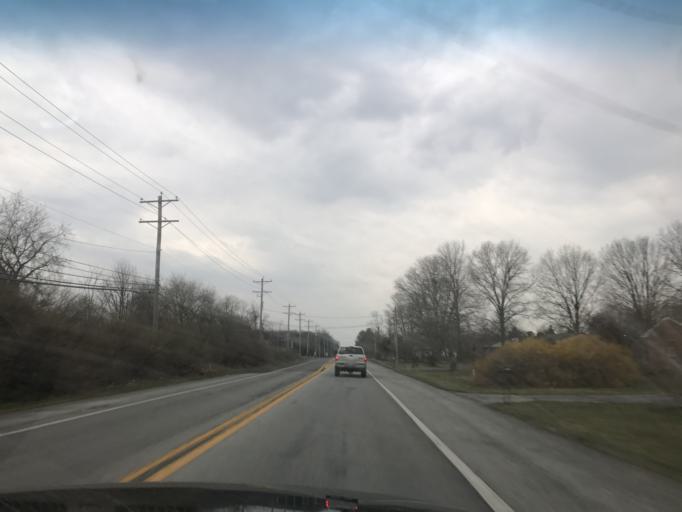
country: US
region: Delaware
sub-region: New Castle County
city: Glasgow
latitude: 39.6249
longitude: -75.7766
